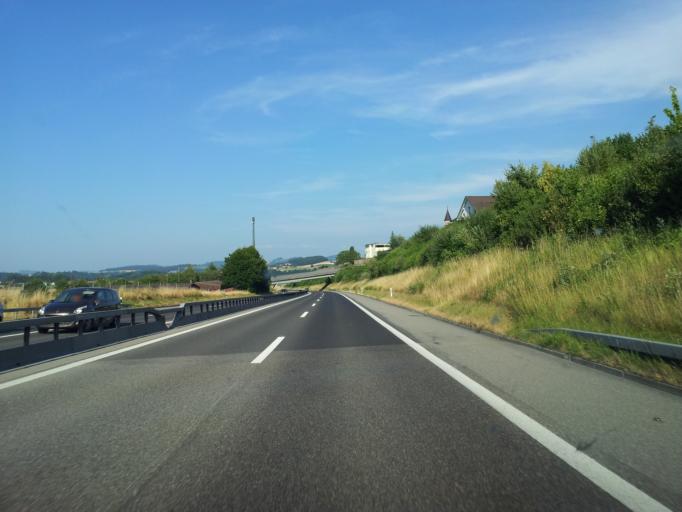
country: CH
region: Fribourg
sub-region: Sense District
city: Schmitten
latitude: 46.8752
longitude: 7.2691
